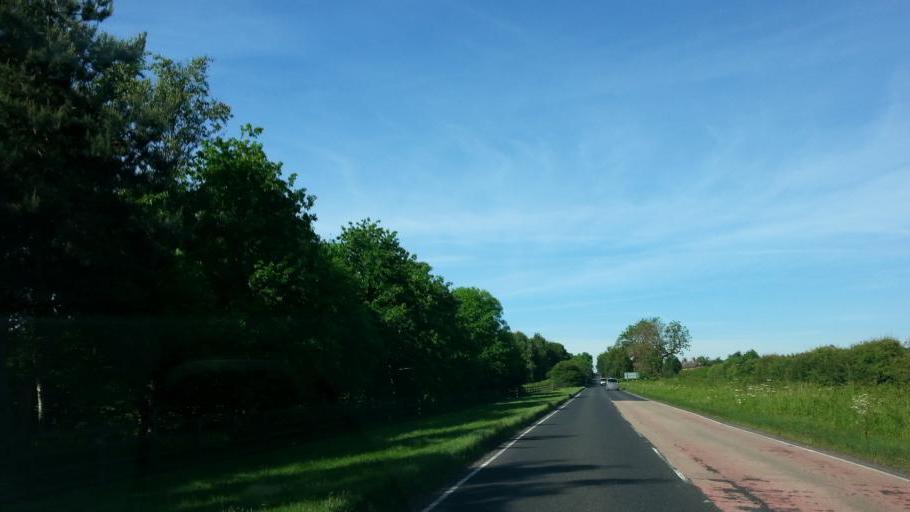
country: GB
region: England
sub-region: Nottinghamshire
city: Arnold
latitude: 53.0411
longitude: -1.1150
